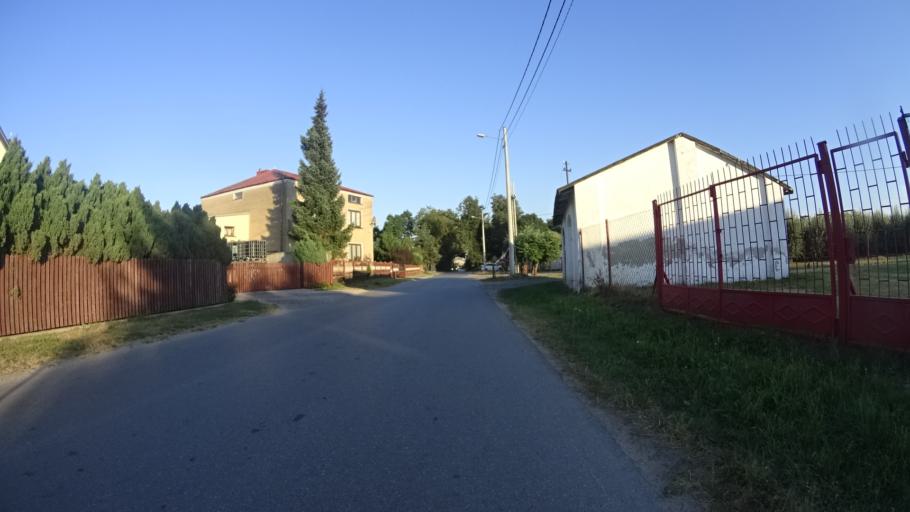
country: PL
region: Masovian Voivodeship
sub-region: Powiat grojecki
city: Goszczyn
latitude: 51.6953
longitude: 20.8135
